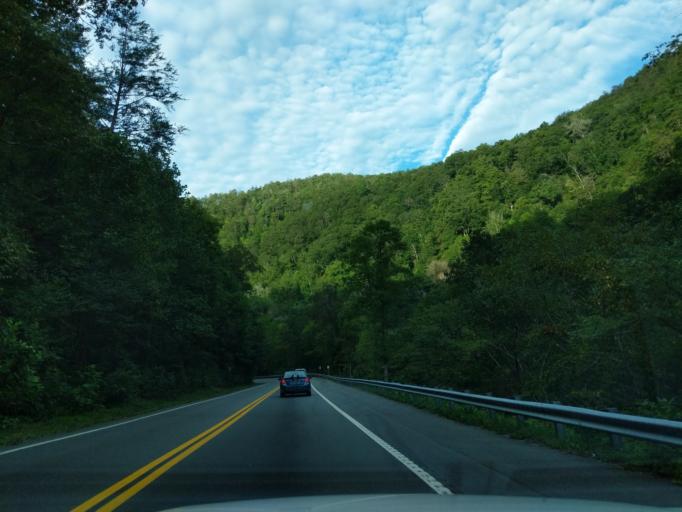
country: US
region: Georgia
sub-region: Fannin County
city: McCaysville
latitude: 35.0773
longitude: -84.5076
